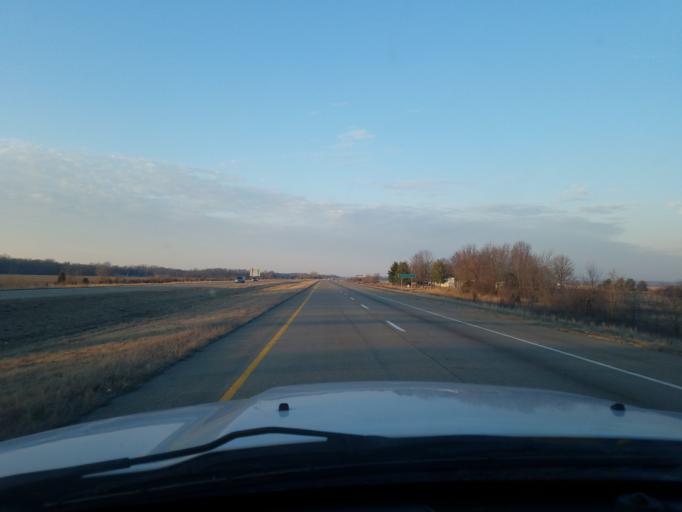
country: US
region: Indiana
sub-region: Vanderburgh County
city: Melody Hill
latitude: 38.0355
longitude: -87.4731
